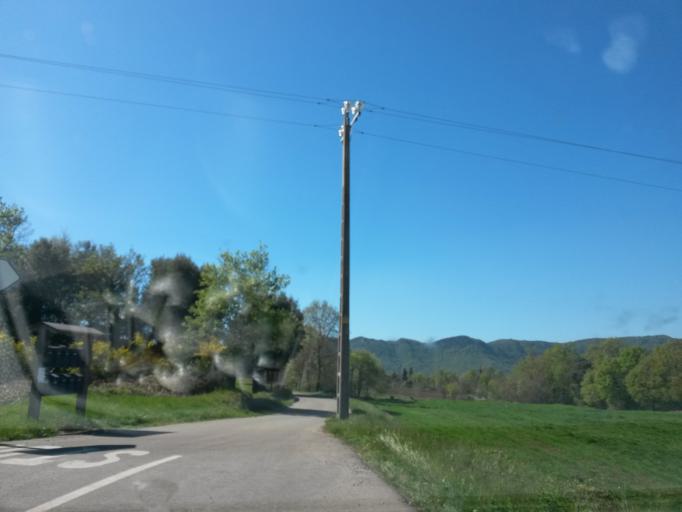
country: ES
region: Catalonia
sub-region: Provincia de Girona
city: Sant Cristofol de les Fonts
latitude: 42.1722
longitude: 2.5192
